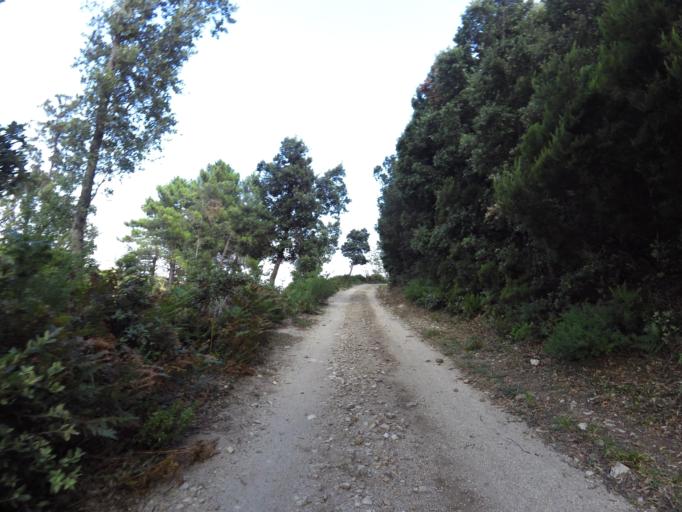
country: IT
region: Calabria
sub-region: Provincia di Reggio Calabria
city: Pazzano
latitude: 38.4775
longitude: 16.4054
